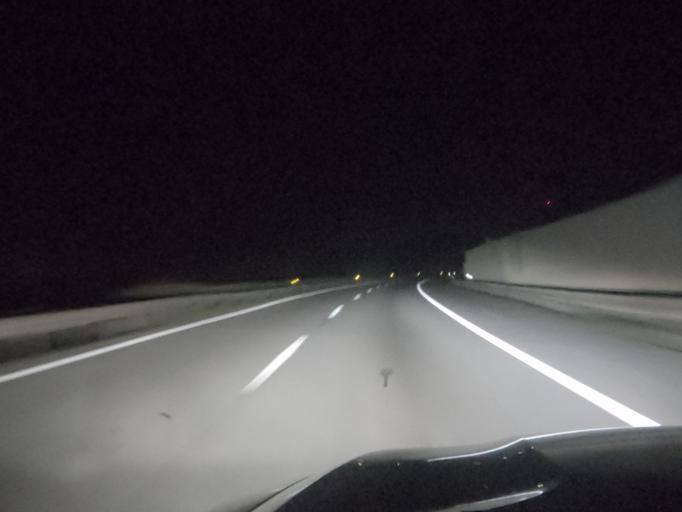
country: PT
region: Aveiro
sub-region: Estarreja
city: Beduido
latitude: 40.7673
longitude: -8.5433
